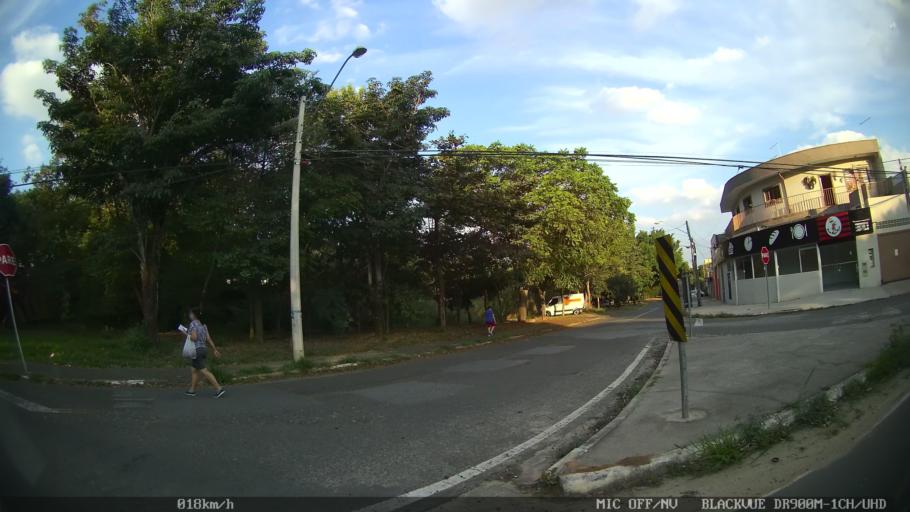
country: BR
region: Sao Paulo
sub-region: Hortolandia
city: Hortolandia
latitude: -22.8952
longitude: -47.1549
